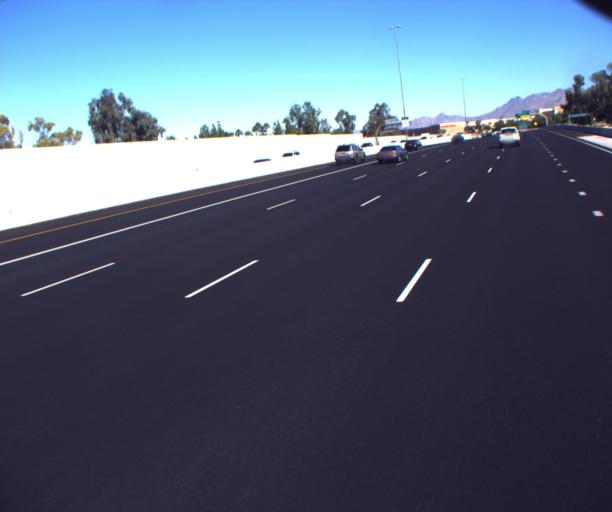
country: US
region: Arizona
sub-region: Maricopa County
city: Scottsdale
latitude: 33.5703
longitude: -111.8903
